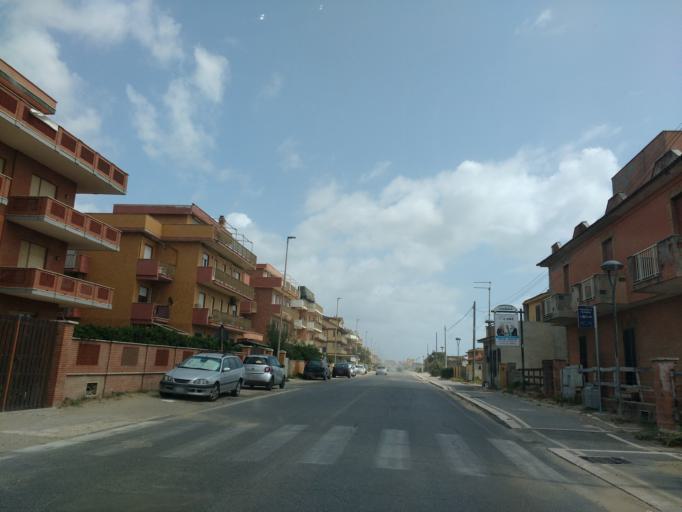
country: IT
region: Latium
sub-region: Citta metropolitana di Roma Capitale
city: Ardea
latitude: 41.5870
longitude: 12.4986
